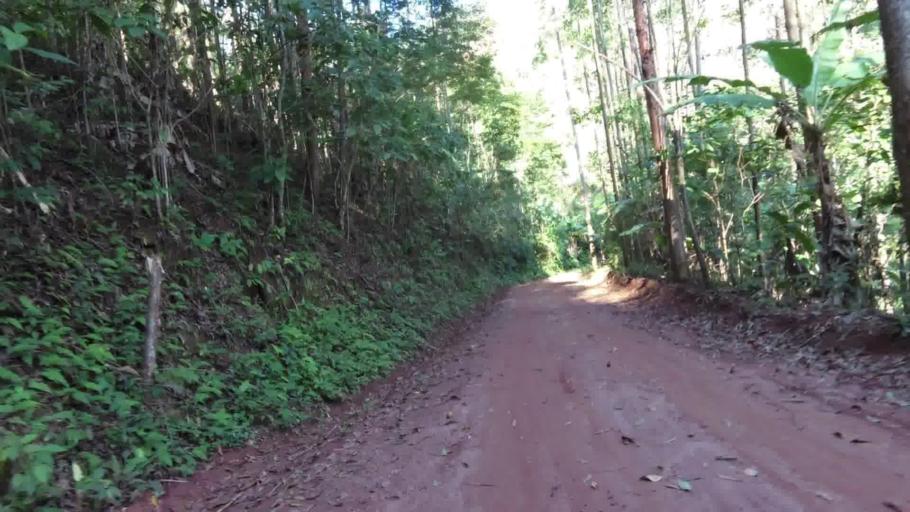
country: BR
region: Espirito Santo
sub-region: Alfredo Chaves
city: Alfredo Chaves
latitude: -20.6063
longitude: -40.7590
